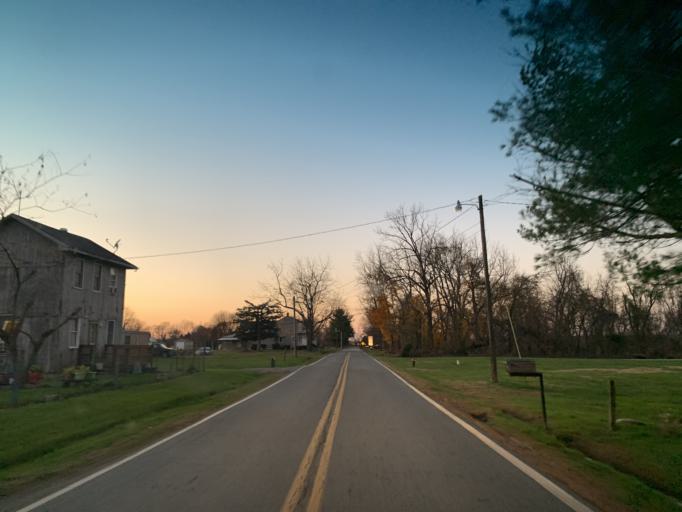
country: US
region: Delaware
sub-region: New Castle County
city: Middletown
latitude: 39.4197
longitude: -75.7760
